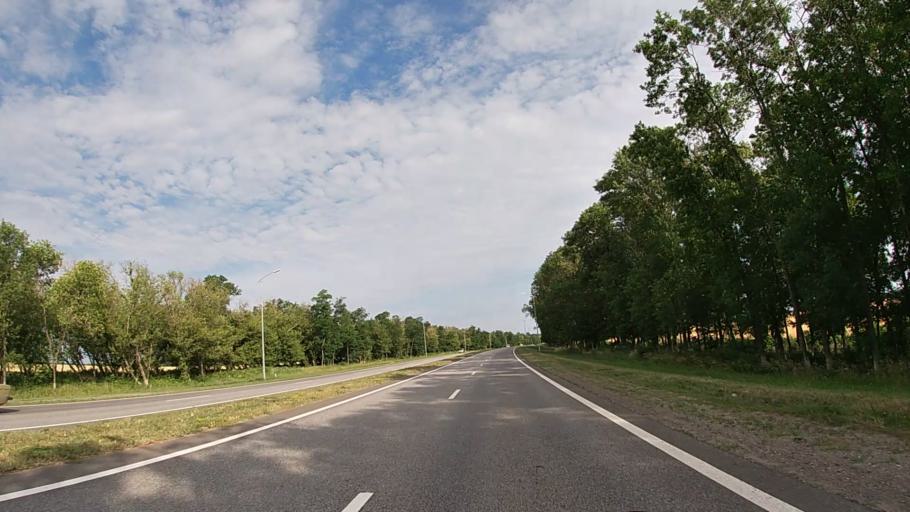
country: RU
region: Belgorod
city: Tomarovka
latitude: 50.6727
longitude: 36.2983
